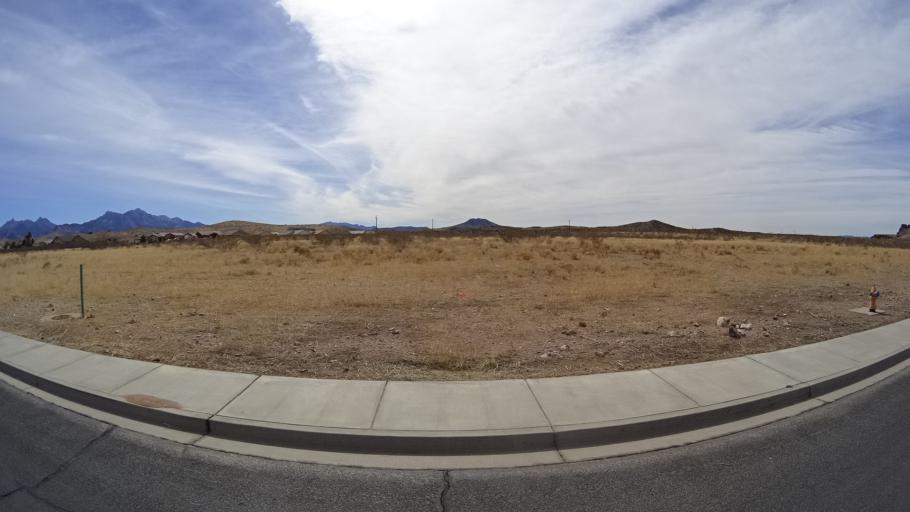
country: US
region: Arizona
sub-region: Mohave County
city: Kingman
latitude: 35.1887
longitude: -114.0193
